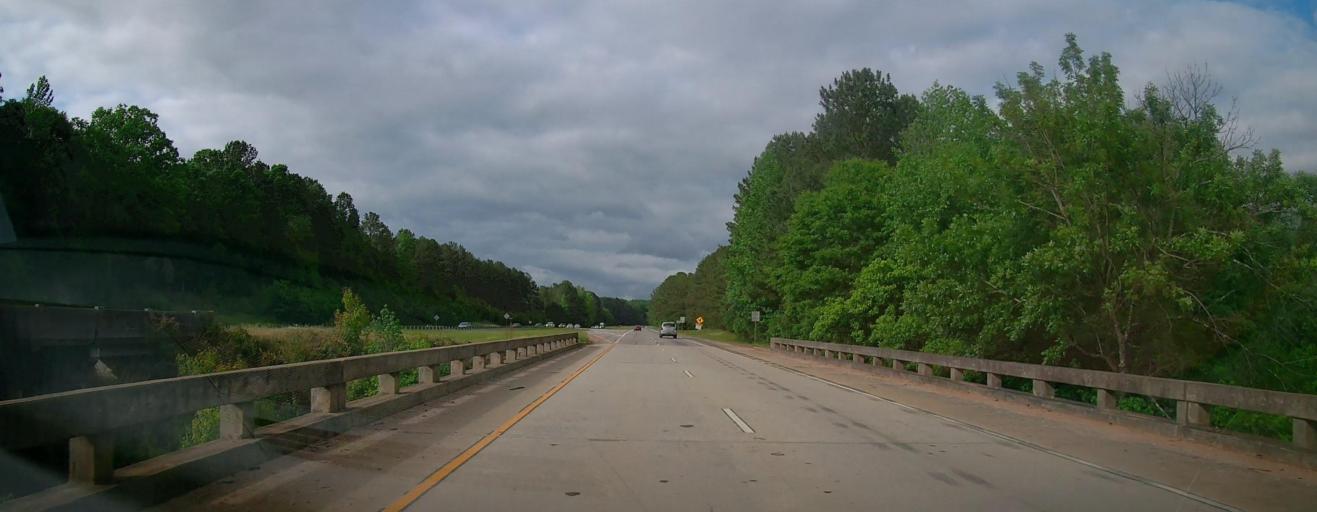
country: US
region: Georgia
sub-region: Barrow County
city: Statham
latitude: 33.8813
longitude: -83.5919
